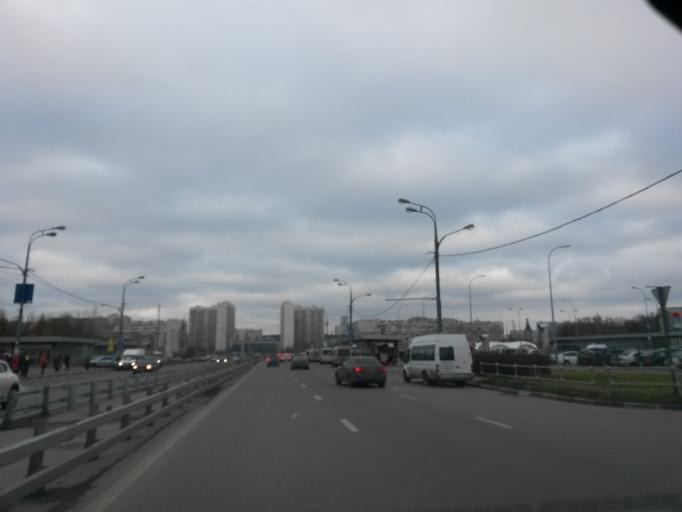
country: RU
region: Moscow
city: Annino
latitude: 55.5696
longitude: 37.5761
